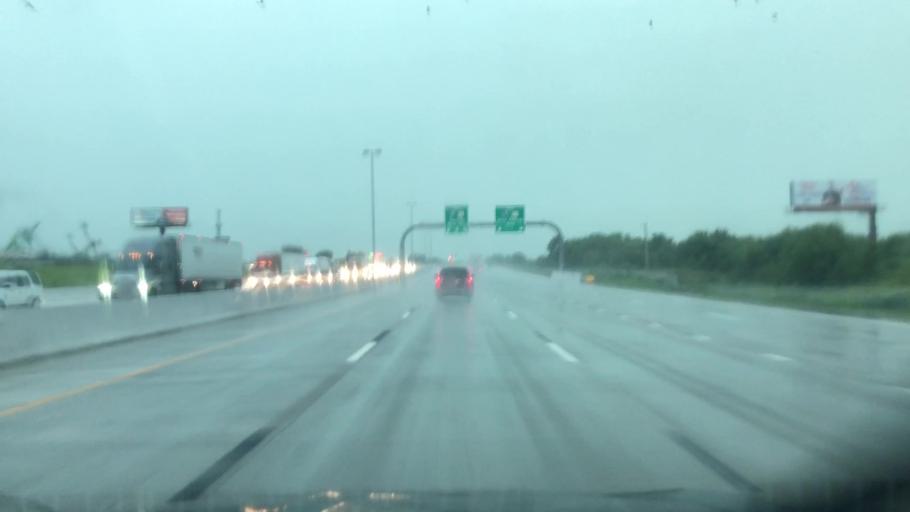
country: US
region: Oklahoma
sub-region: Rogers County
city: Catoosa
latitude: 36.1626
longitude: -95.8167
